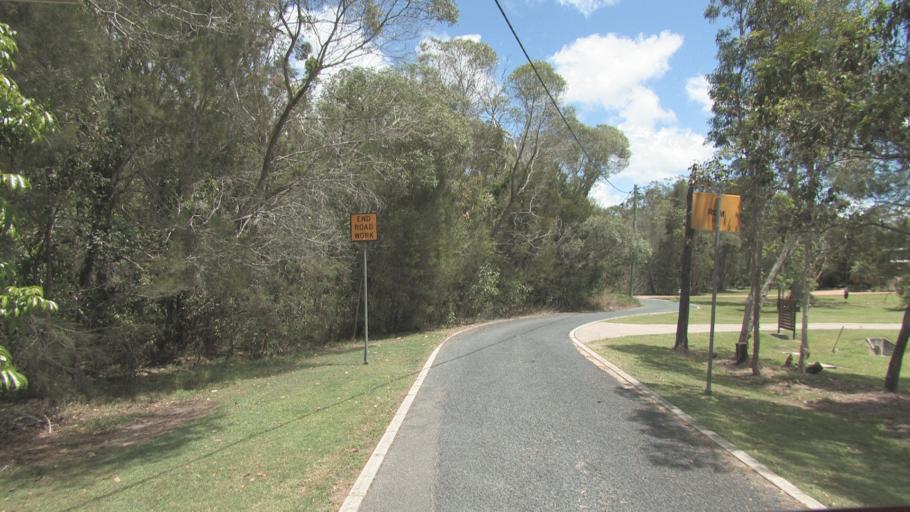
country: AU
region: Queensland
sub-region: Logan
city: Beenleigh
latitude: -27.6573
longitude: 153.2269
